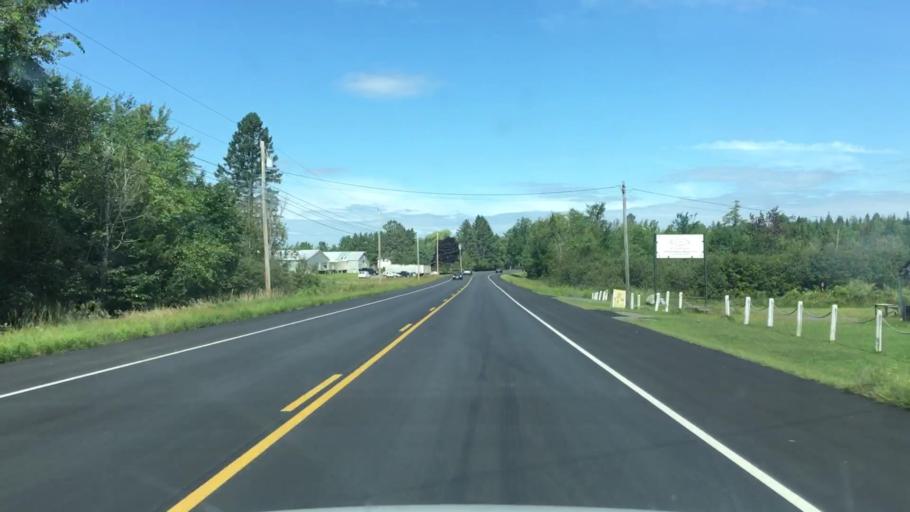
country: US
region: Maine
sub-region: Penobscot County
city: Corinna
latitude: 44.9668
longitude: -69.2734
